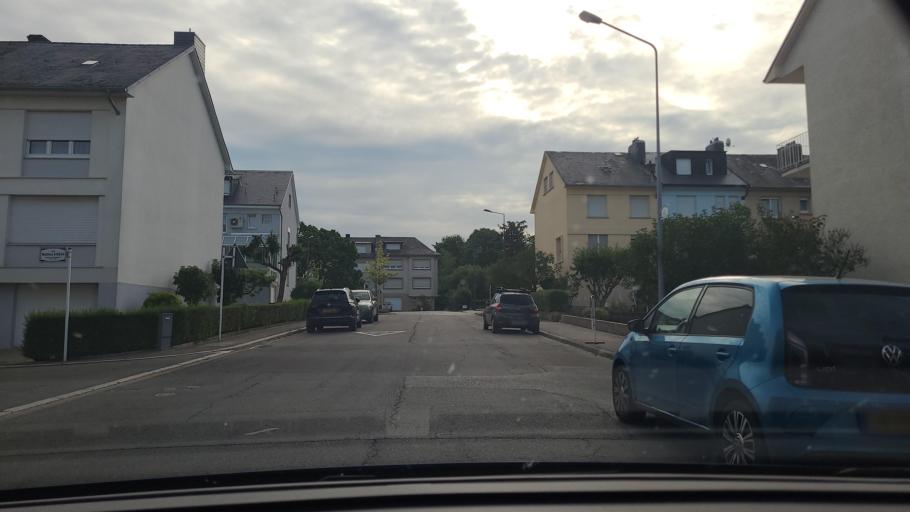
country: LU
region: Luxembourg
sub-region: Canton de Luxembourg
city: Luxembourg
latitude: 49.5935
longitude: 6.1459
